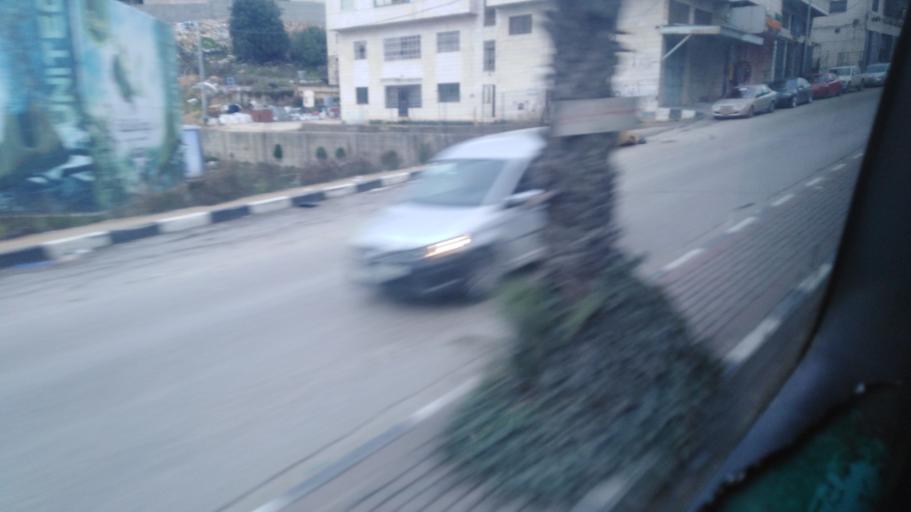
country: PS
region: West Bank
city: Hebron
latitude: 31.5284
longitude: 35.0888
